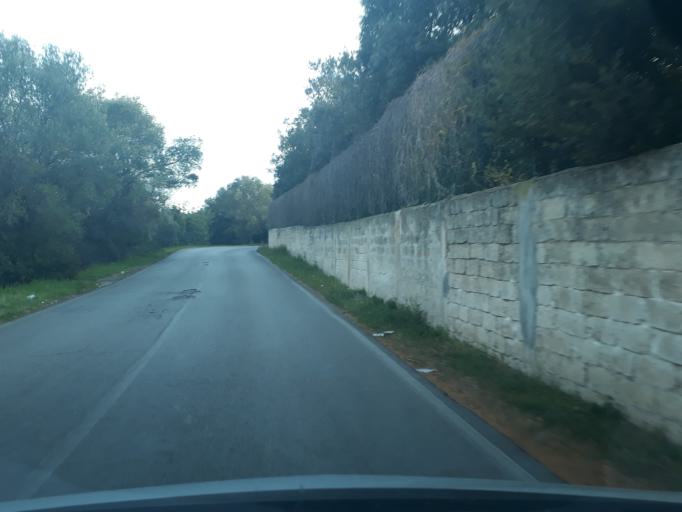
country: IT
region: Apulia
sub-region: Provincia di Brindisi
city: Lamie di Olimpie-Selva
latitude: 40.8318
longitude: 17.3411
